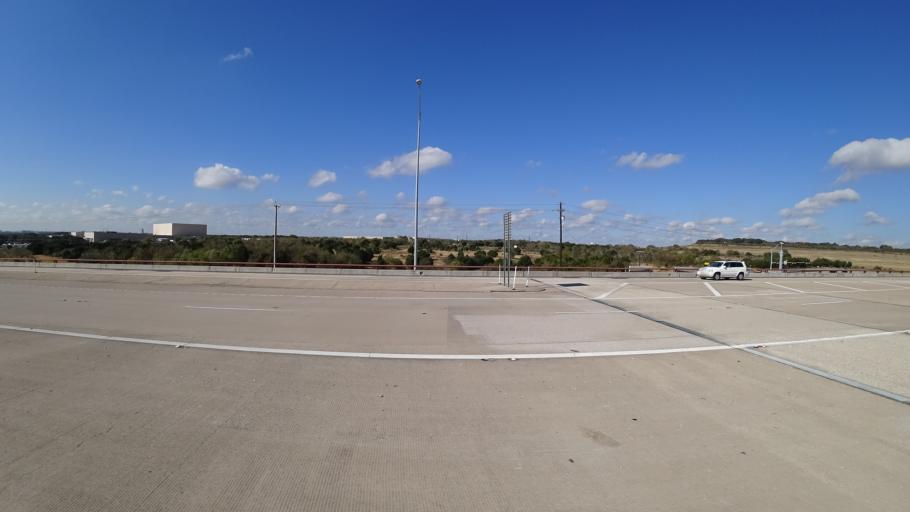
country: US
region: Texas
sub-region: Travis County
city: Wells Branch
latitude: 30.4495
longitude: -97.6964
